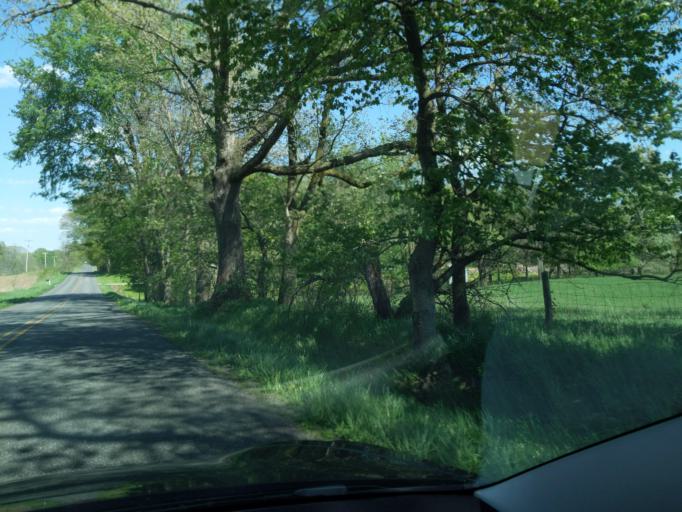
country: US
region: Michigan
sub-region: Barry County
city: Middleville
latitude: 42.7981
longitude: -85.3944
